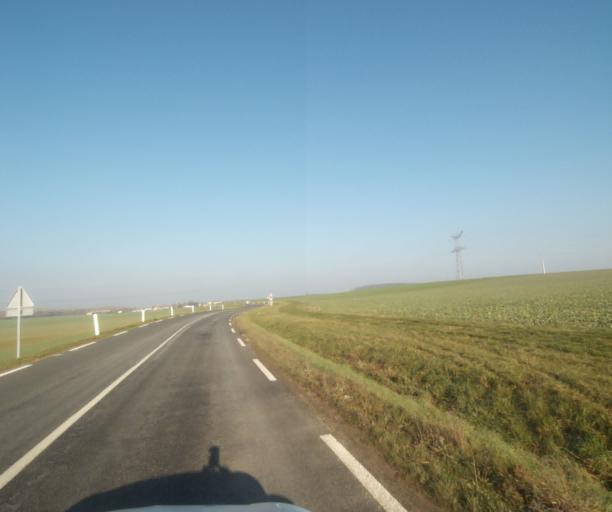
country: FR
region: Champagne-Ardenne
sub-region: Departement de la Haute-Marne
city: Wassy
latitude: 48.5148
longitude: 4.9362
